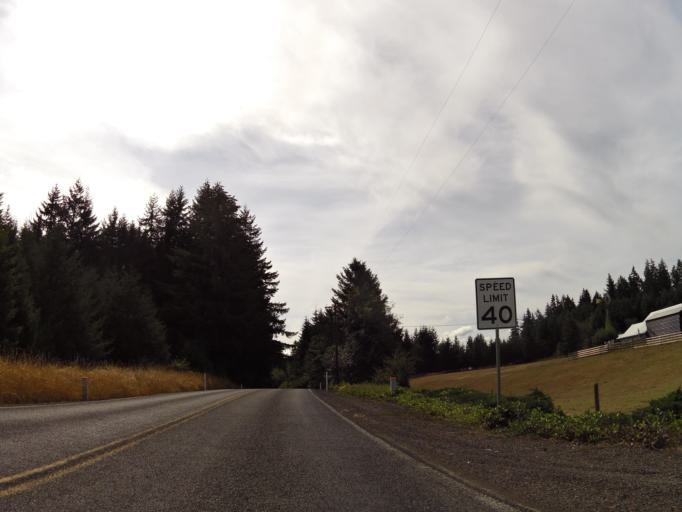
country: US
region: Washington
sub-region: Lewis County
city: Chehalis
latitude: 46.5978
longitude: -122.9712
